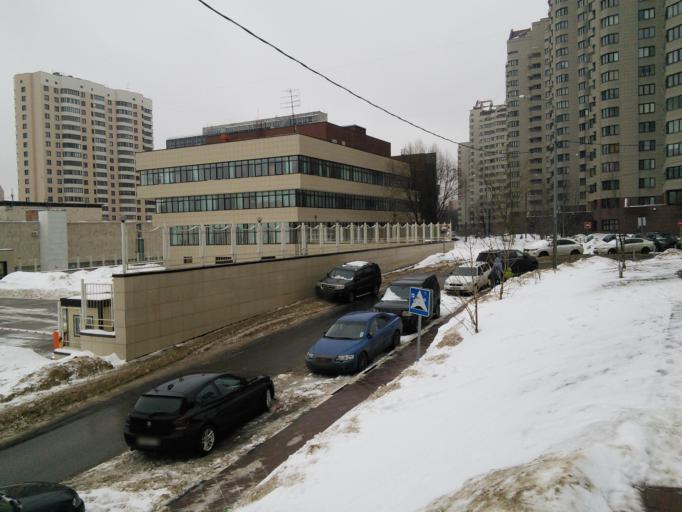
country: RU
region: Moskovskaya
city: Cheremushki
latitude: 55.6745
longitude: 37.5629
